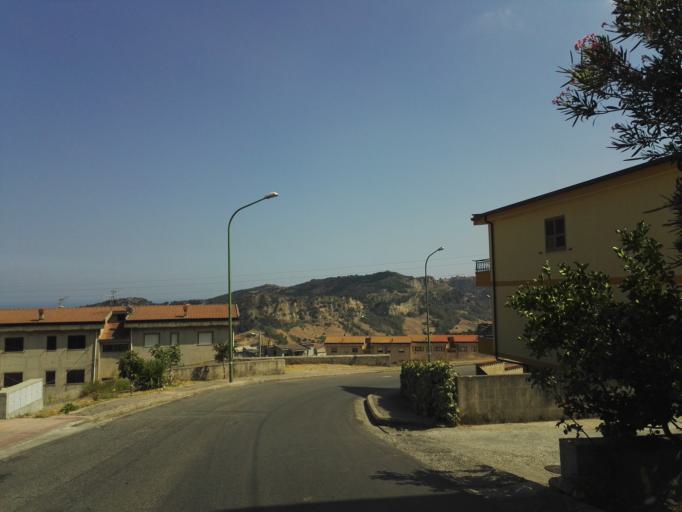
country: IT
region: Calabria
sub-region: Provincia di Reggio Calabria
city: Stilo
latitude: 38.4740
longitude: 16.4650
